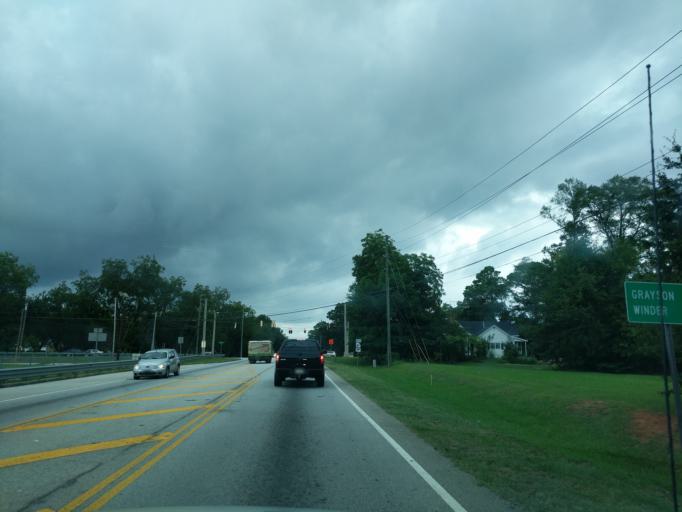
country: US
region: Georgia
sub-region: Walton County
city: Loganville
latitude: 33.8433
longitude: -83.8976
